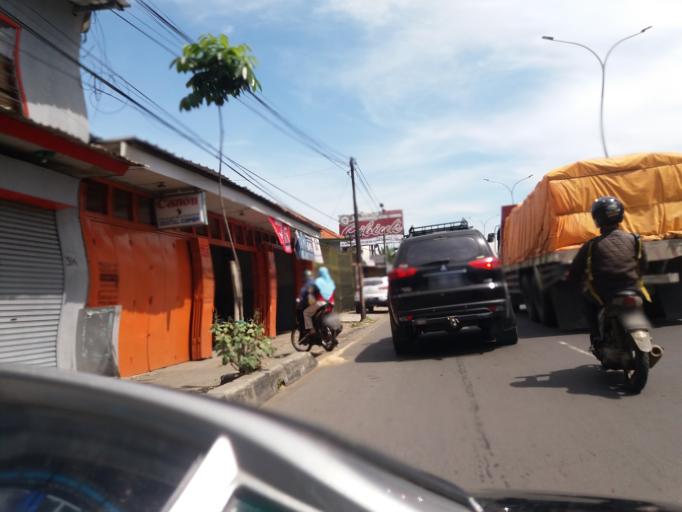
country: ID
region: West Java
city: Bandung
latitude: -6.9463
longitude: 107.6390
